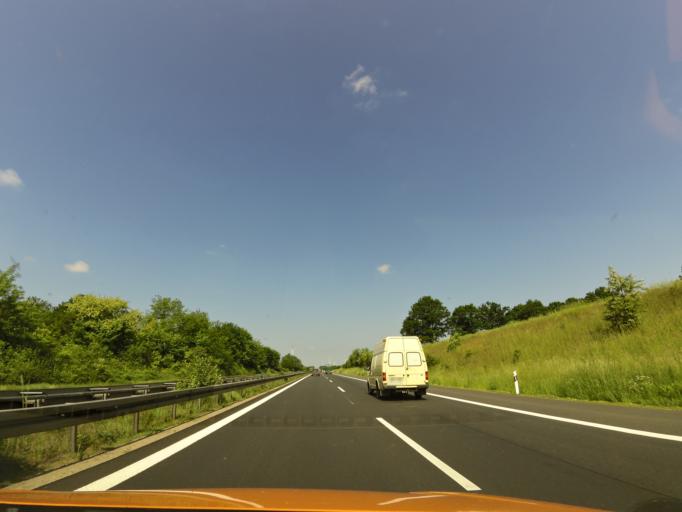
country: DE
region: Brandenburg
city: Gerdshagen
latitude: 53.2055
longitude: 12.2614
